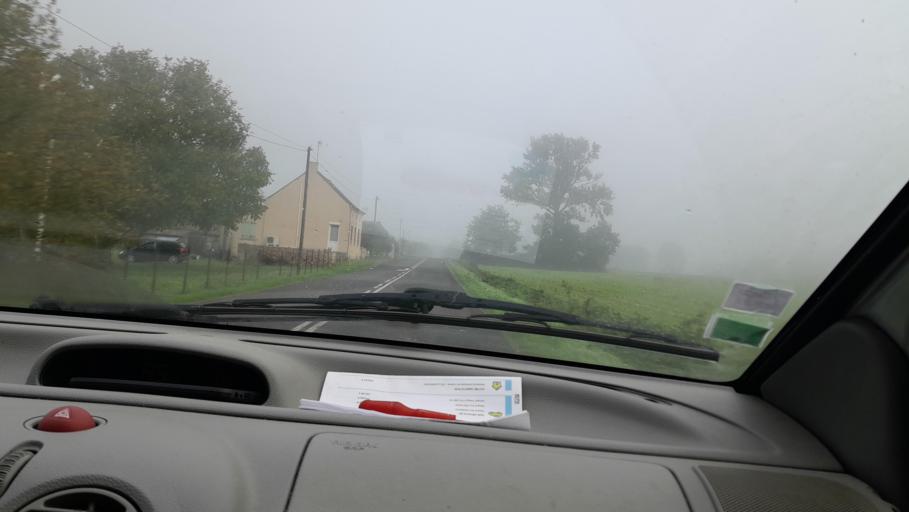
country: FR
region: Brittany
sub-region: Departement d'Ille-et-Vilaine
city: Le Pertre
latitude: 47.9861
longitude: -1.0411
